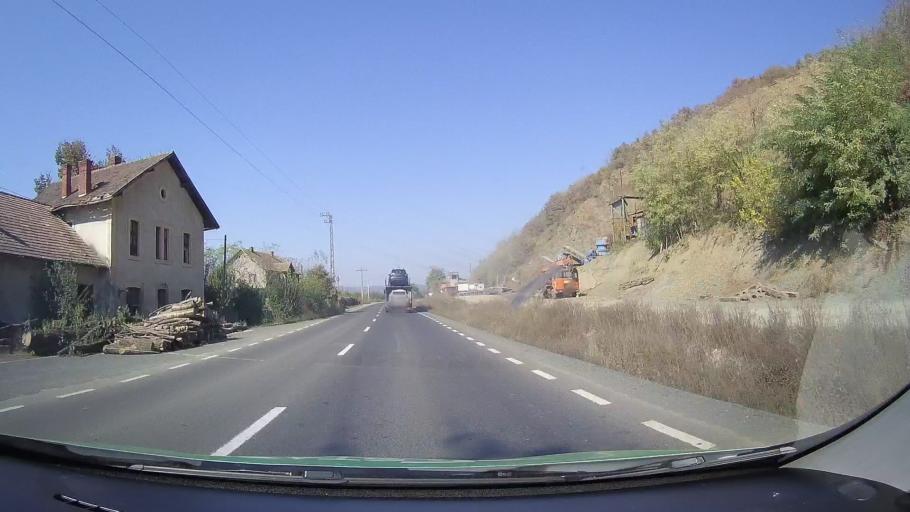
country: RO
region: Arad
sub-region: Comuna Bata
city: Bata
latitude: 46.0558
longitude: 22.0469
